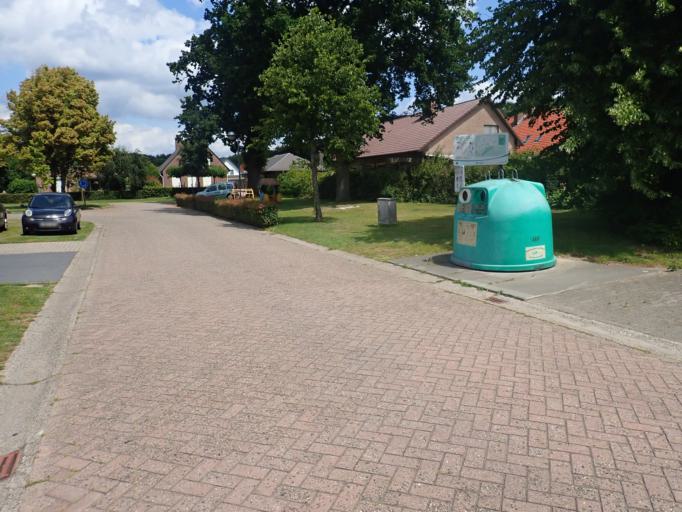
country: BE
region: Flanders
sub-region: Provincie Antwerpen
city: Wuustwezel
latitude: 51.3929
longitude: 4.6021
